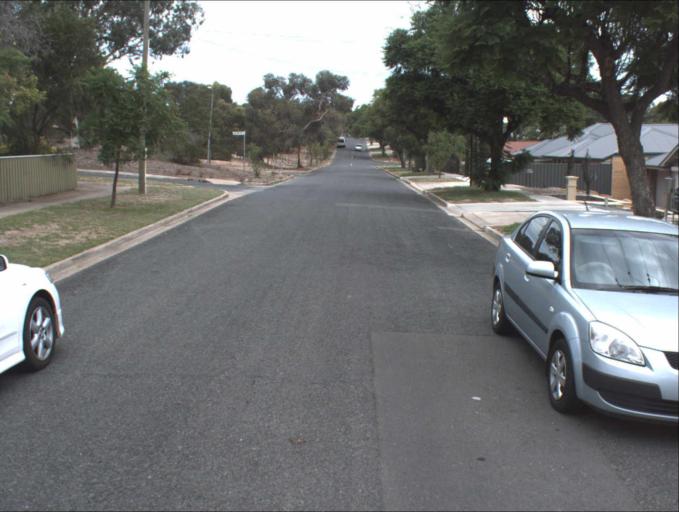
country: AU
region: South Australia
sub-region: Port Adelaide Enfield
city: Enfield
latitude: -34.8558
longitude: 138.6061
